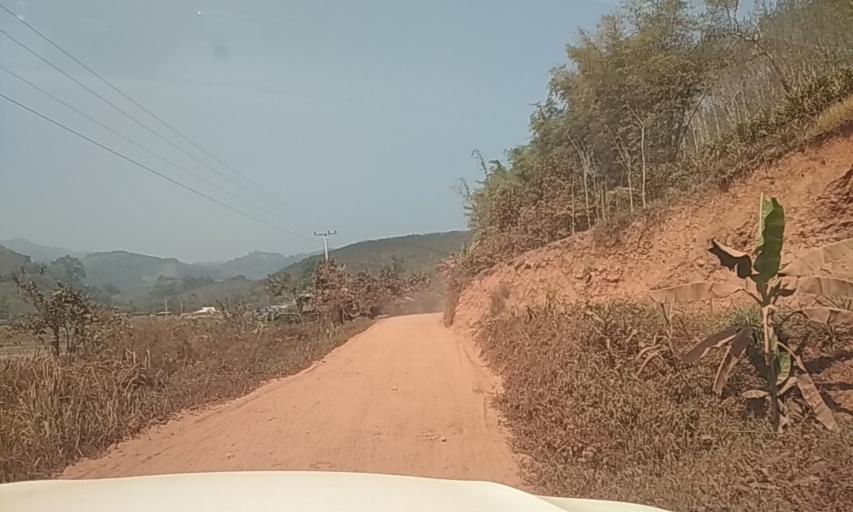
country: CN
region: Yunnan
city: Mengla
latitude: 21.5169
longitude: 101.8493
